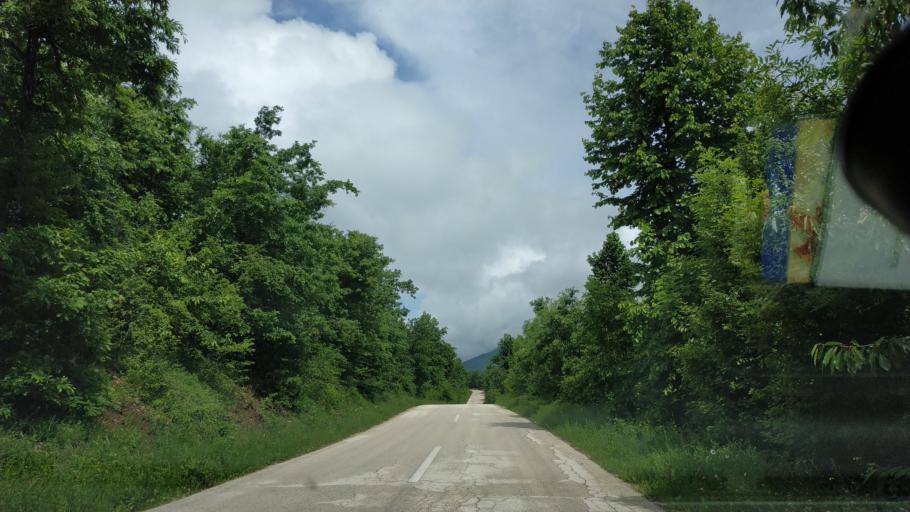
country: RS
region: Central Serbia
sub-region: Zajecarski Okrug
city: Boljevac
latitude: 43.7332
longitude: 21.9533
